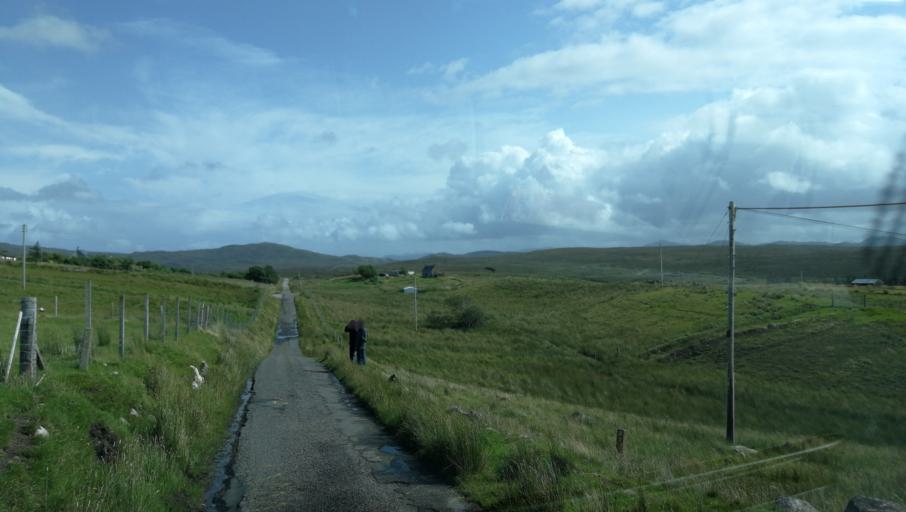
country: GB
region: Scotland
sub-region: Highland
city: Portree
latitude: 57.7473
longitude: -5.7745
